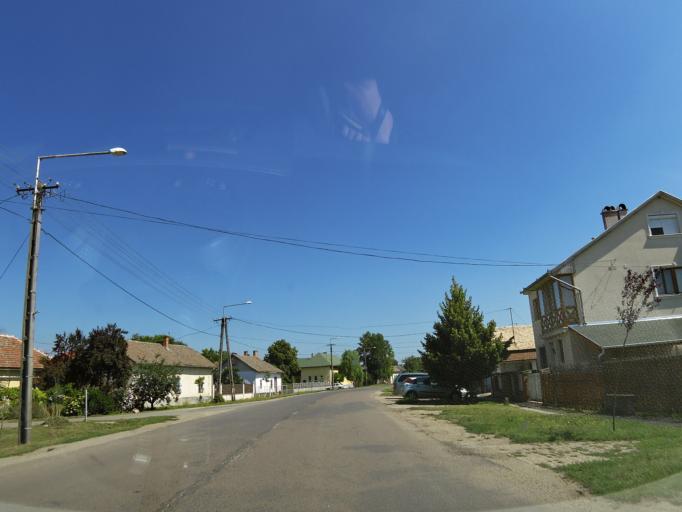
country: HU
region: Jasz-Nagykun-Szolnok
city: Kunhegyes
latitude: 47.3628
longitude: 20.6258
